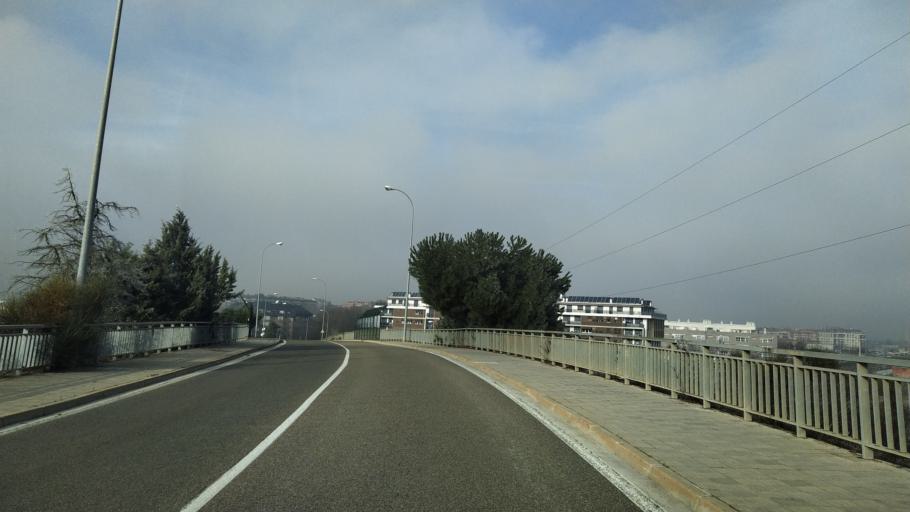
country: ES
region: Castille and Leon
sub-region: Provincia de Palencia
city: Palencia
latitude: 41.9935
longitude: -4.5139
